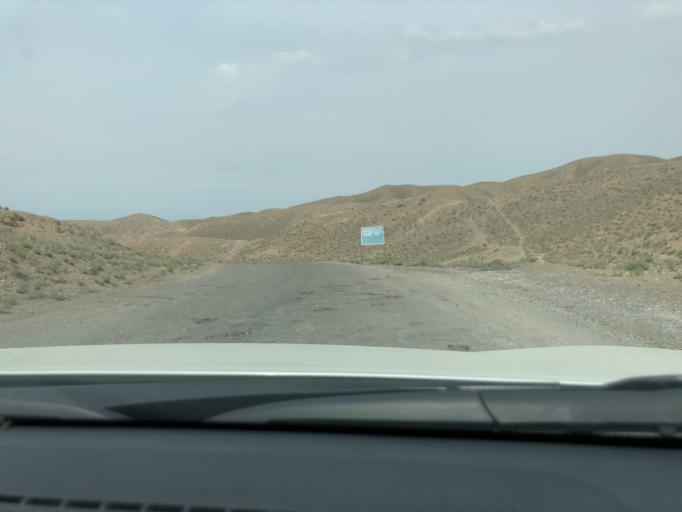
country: TJ
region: Viloyati Sughd
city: Kim
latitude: 40.2175
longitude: 70.4797
